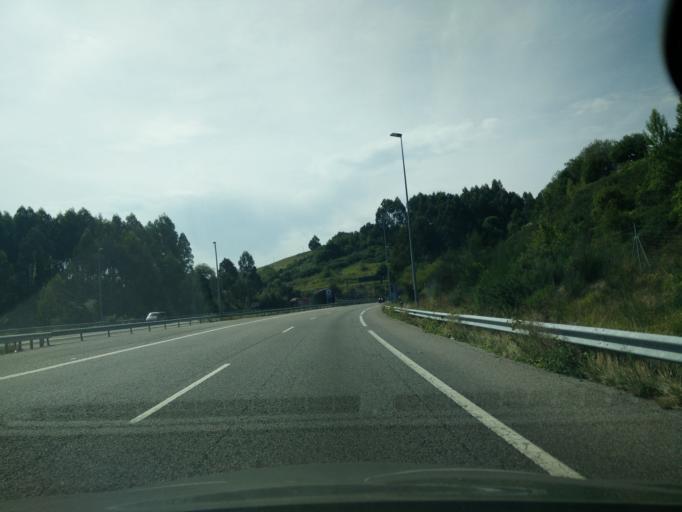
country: ES
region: Asturias
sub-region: Province of Asturias
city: Ribadesella
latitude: 43.4408
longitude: -5.0874
